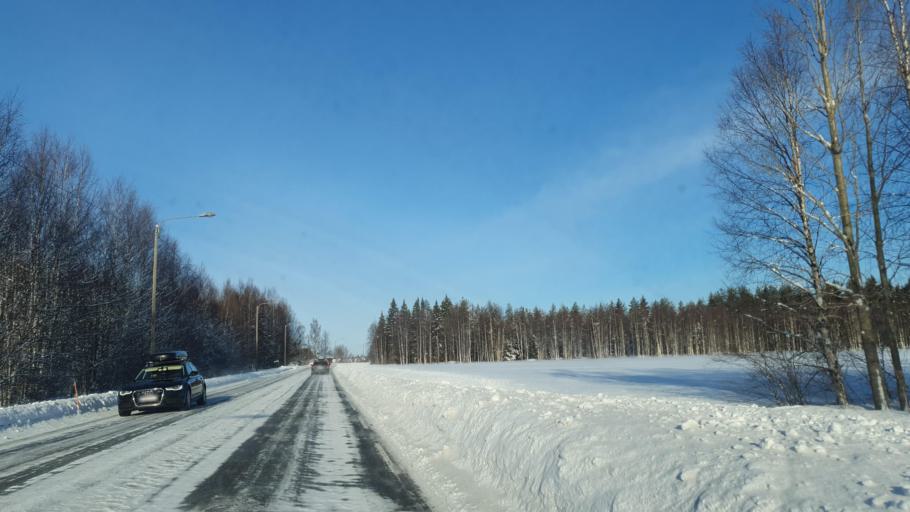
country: FI
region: Lapland
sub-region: Kemi-Tornio
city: Tornio
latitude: 66.0949
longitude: 23.9469
